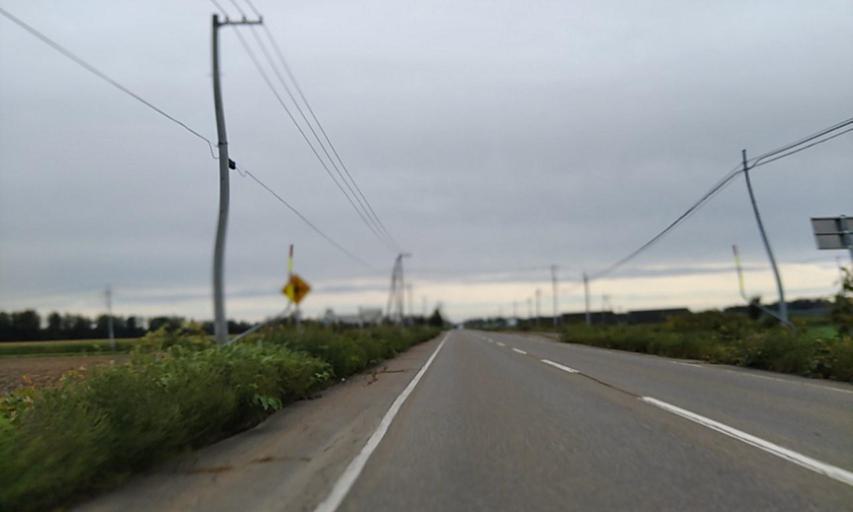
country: JP
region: Hokkaido
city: Obihiro
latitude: 42.6855
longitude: 143.1371
